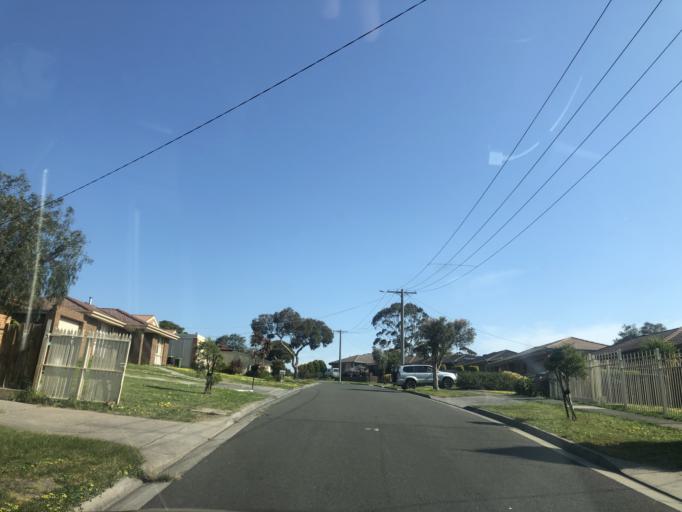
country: AU
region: Victoria
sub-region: Casey
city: Lynbrook
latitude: -38.0433
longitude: 145.2712
